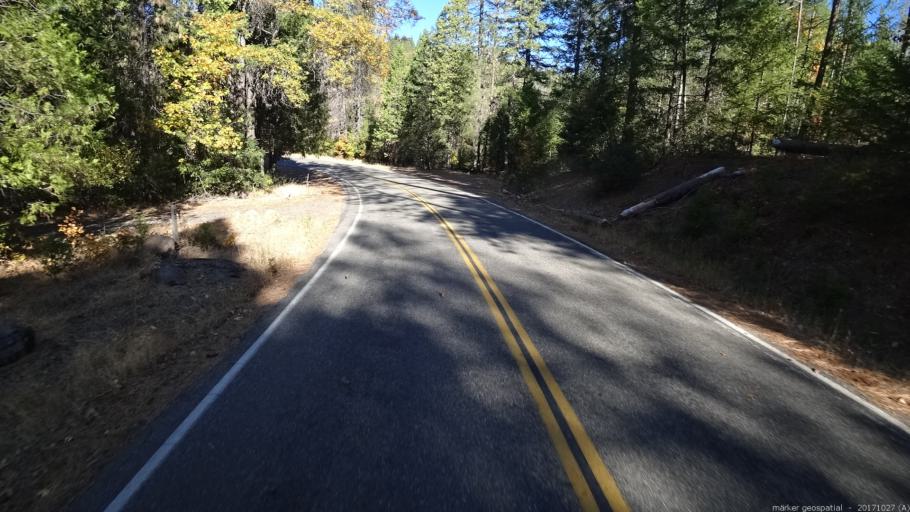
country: US
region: California
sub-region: Shasta County
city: Shingletown
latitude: 40.7017
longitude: -121.9191
